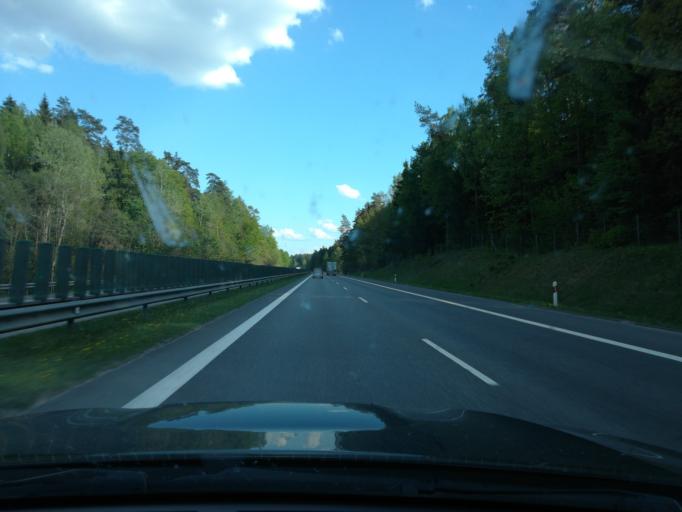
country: LT
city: Trakai
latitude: 54.7245
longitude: 24.9648
